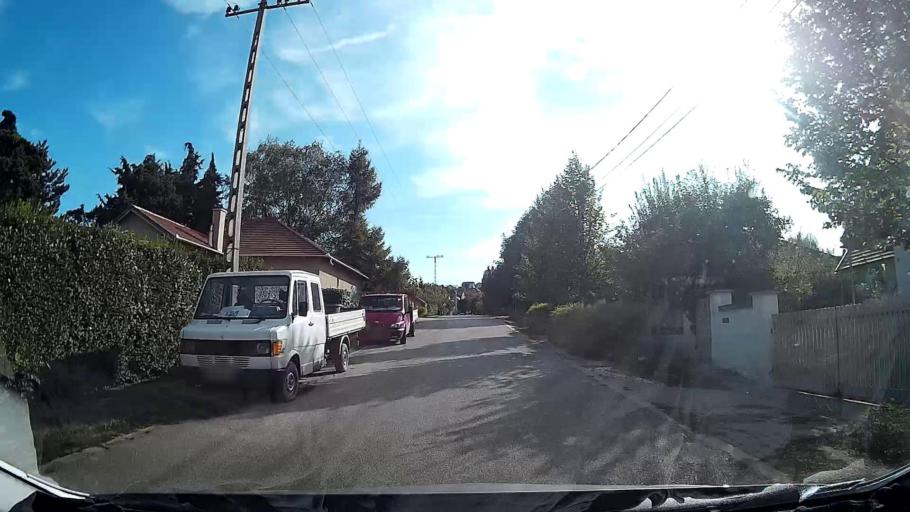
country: HU
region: Pest
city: Pomaz
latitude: 47.6433
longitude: 19.0238
